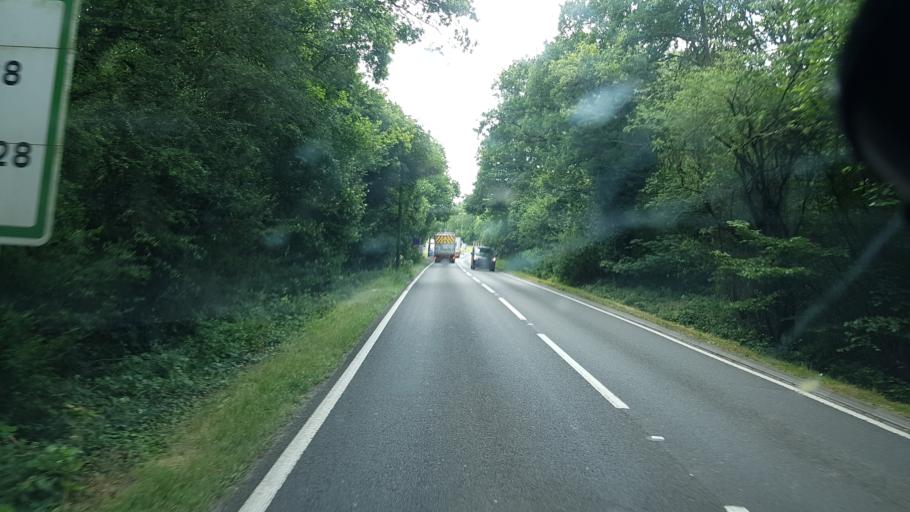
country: GB
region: England
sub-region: Surrey
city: Felbridge
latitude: 51.1662
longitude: -0.0500
